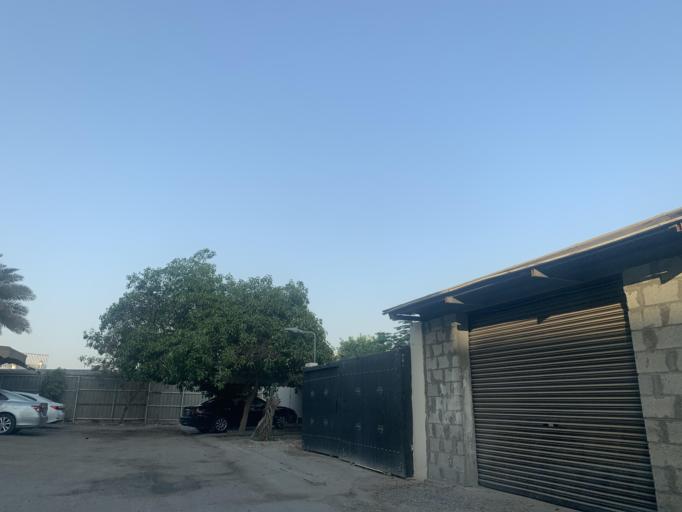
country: BH
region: Manama
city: Jidd Hafs
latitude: 26.2143
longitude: 50.5330
